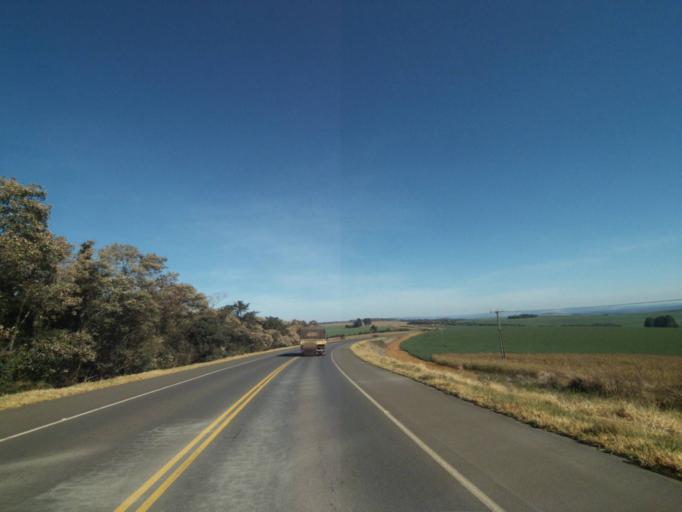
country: BR
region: Parana
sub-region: Tibagi
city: Tibagi
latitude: -24.3774
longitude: -50.3269
